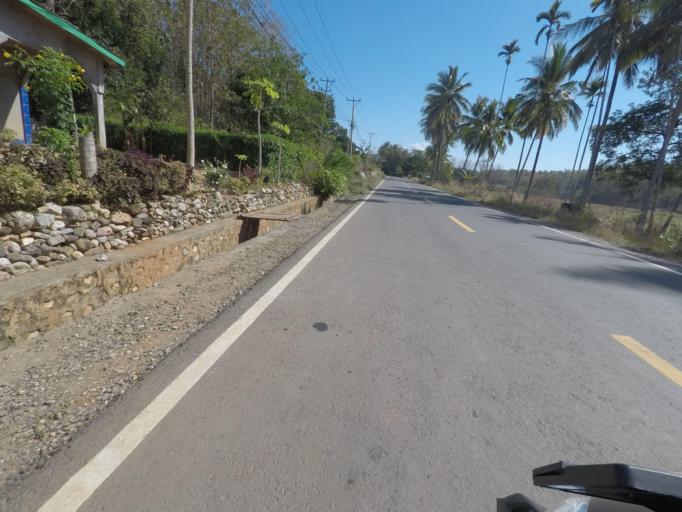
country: TL
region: Bobonaro
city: Maliana
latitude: -8.9557
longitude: 125.2125
